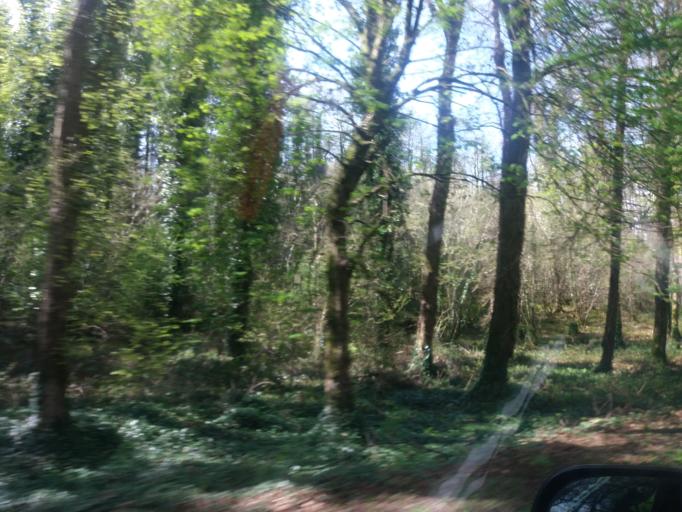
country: GB
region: Northern Ireland
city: Irvinestown
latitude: 54.4124
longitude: -7.7260
